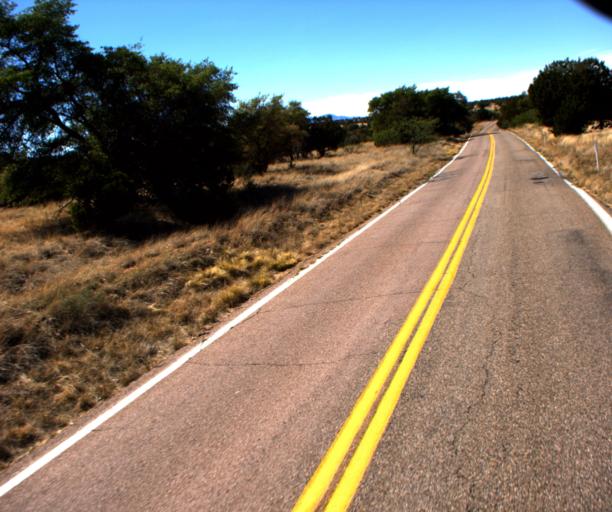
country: US
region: Arizona
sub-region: Cochise County
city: Huachuca City
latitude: 31.5580
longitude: -110.5521
